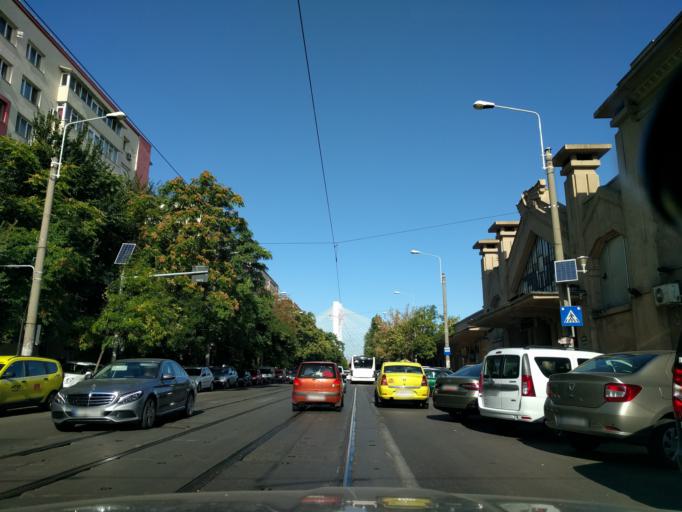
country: RO
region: Bucuresti
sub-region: Municipiul Bucuresti
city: Bucuresti
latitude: 44.4461
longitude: 26.0735
